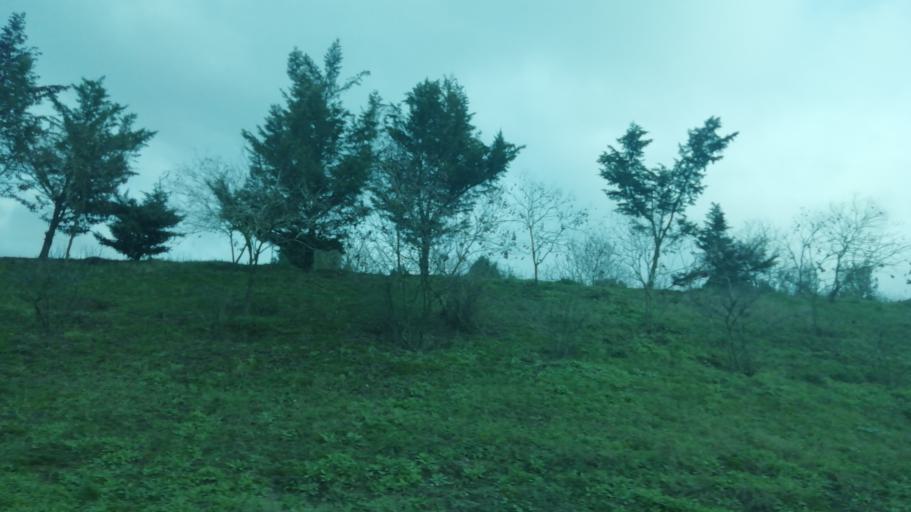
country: TR
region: Istanbul
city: Sisli
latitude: 41.0922
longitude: 28.9382
